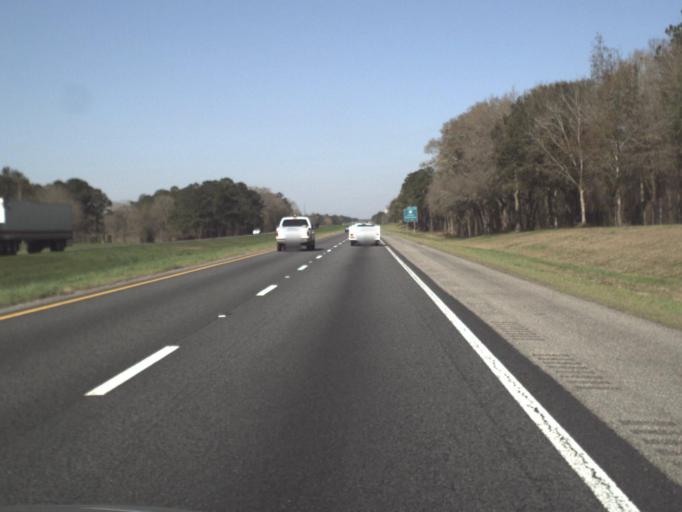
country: US
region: Florida
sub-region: Gadsden County
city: Gretna
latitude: 30.5713
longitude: -84.6756
